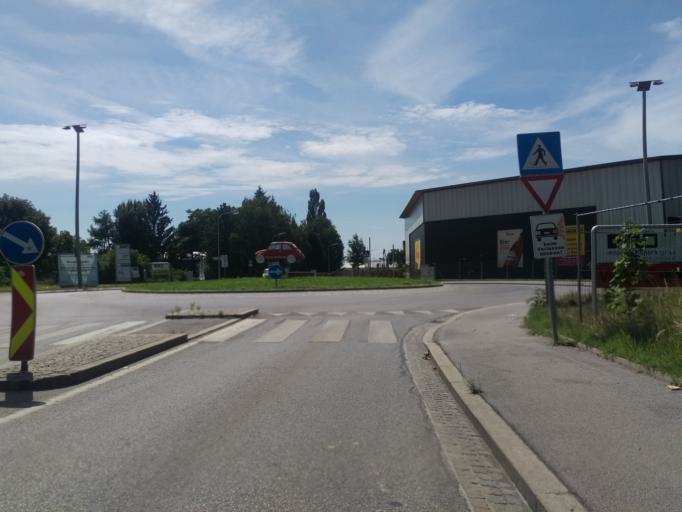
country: AT
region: Styria
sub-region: Graz Stadt
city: Graz
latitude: 47.0435
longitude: 15.4373
